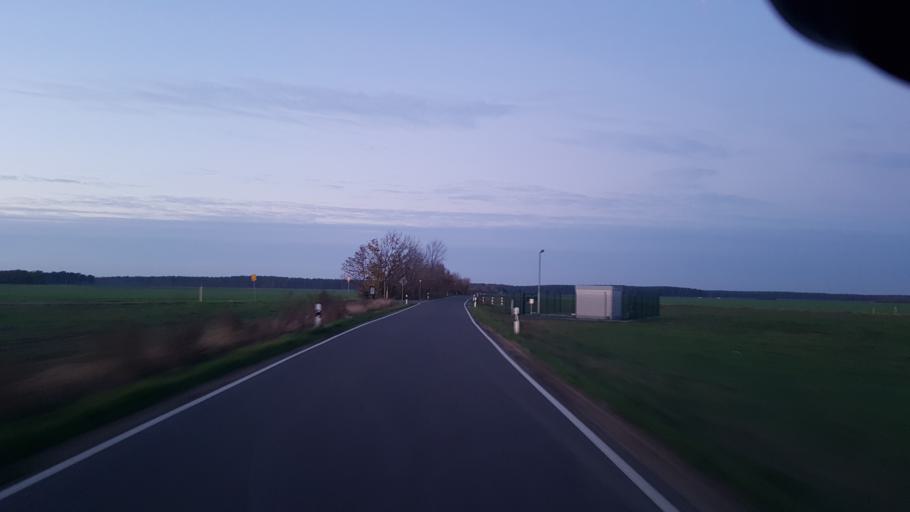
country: DE
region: Saxony
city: Arzberg
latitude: 51.5382
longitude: 13.1354
